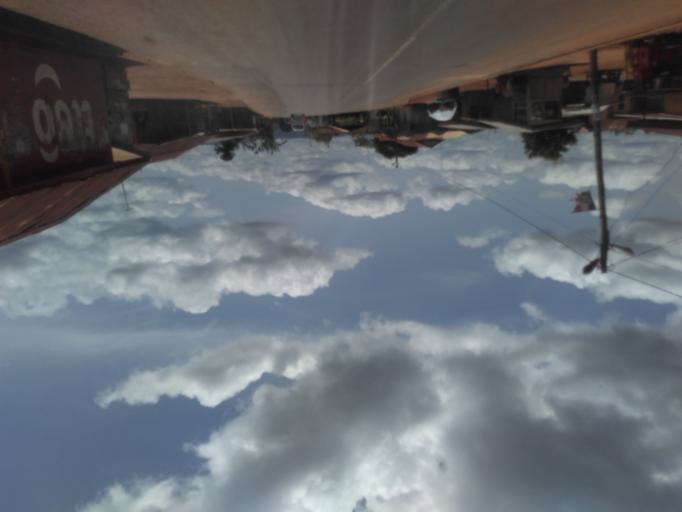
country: GH
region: Eastern
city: Koforidua
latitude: 6.1121
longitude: -0.1231
